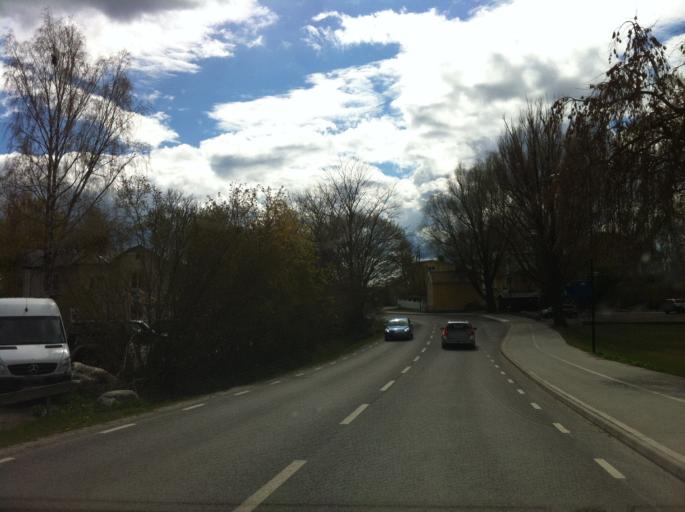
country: SE
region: Stockholm
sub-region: Vaxholms Kommun
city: Vaxholm
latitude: 59.4033
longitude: 18.3414
